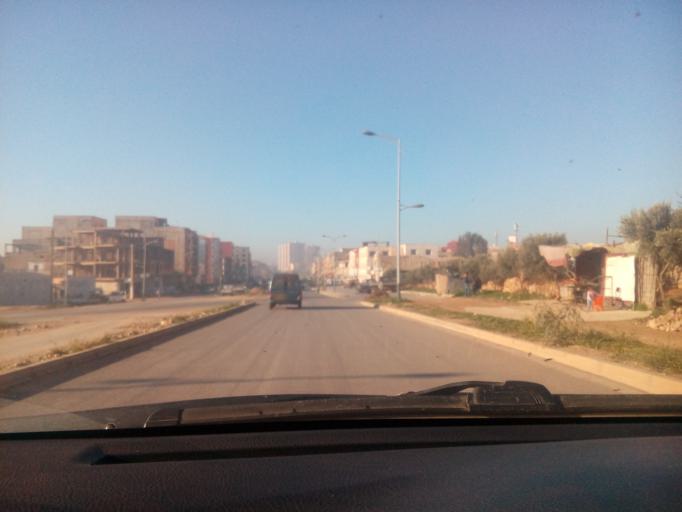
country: DZ
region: Oran
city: Bir el Djir
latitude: 35.7537
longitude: -0.5456
